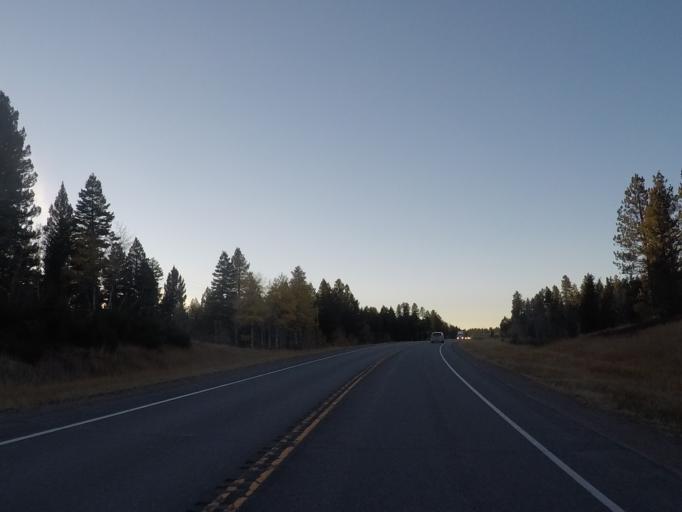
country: US
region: Montana
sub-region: Lewis and Clark County
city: Lincoln
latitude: 47.0092
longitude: -113.0590
